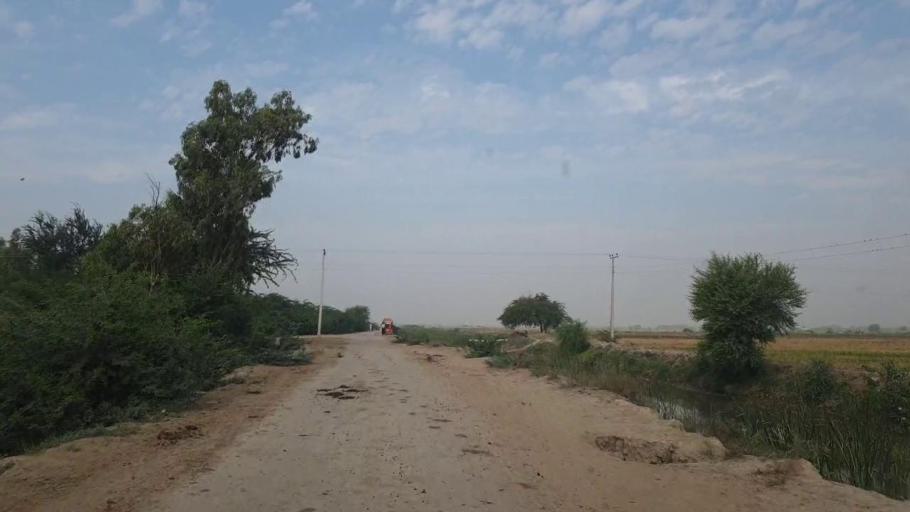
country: PK
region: Sindh
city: Tando Bago
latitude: 24.8636
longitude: 68.9946
